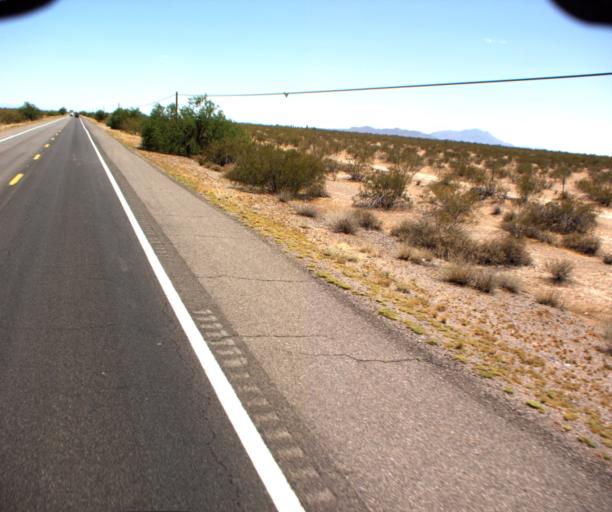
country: US
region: Arizona
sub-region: Pinal County
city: Florence
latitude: 32.9958
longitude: -111.3671
